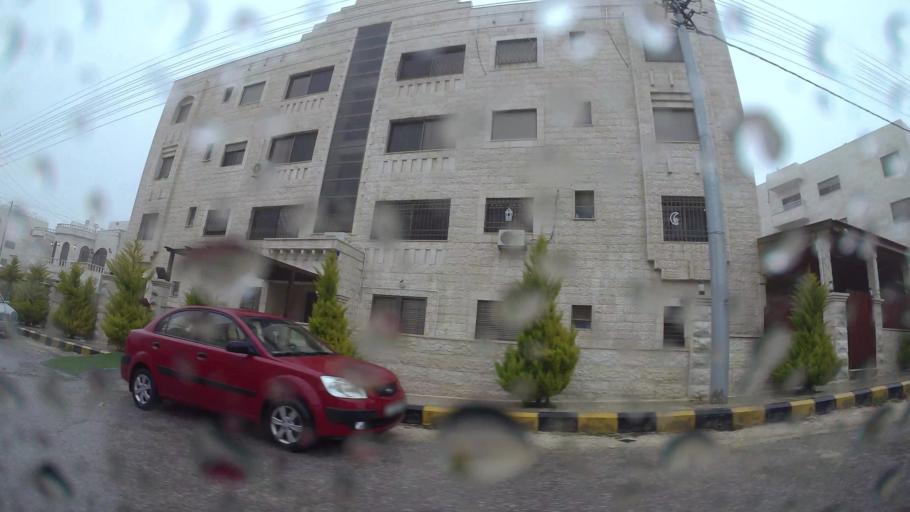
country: JO
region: Amman
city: Al Jubayhah
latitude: 32.0133
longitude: 35.8879
